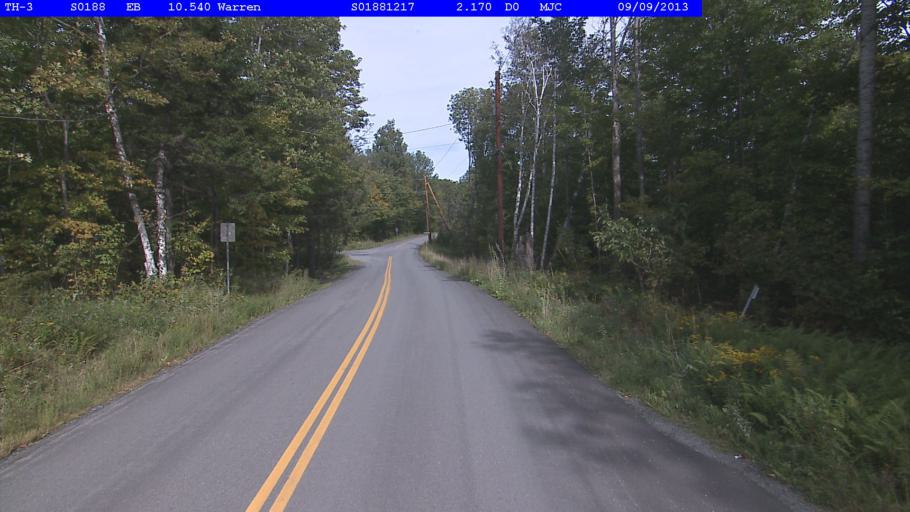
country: US
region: Vermont
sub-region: Addison County
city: Bristol
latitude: 44.1015
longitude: -72.8890
